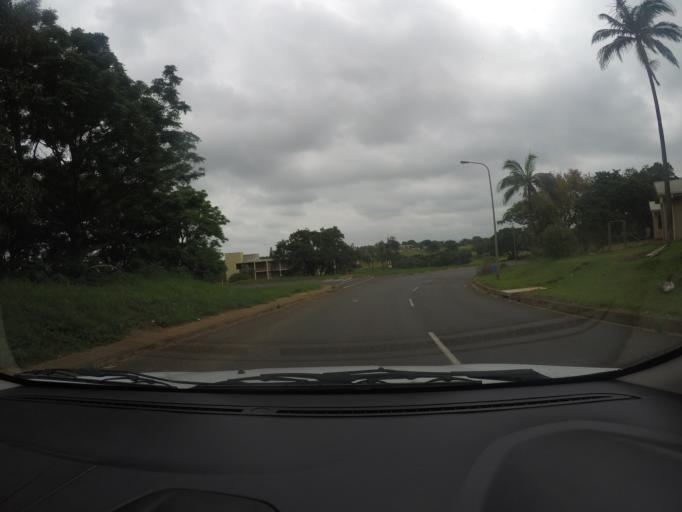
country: ZA
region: KwaZulu-Natal
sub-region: uThungulu District Municipality
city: Empangeni
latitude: -28.7469
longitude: 31.8876
